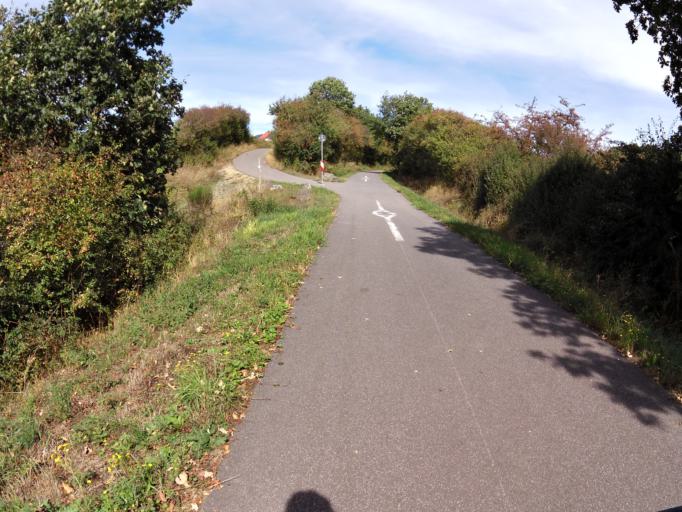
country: DE
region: Rheinland-Pfalz
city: Arzfeld
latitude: 50.0813
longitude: 6.2712
